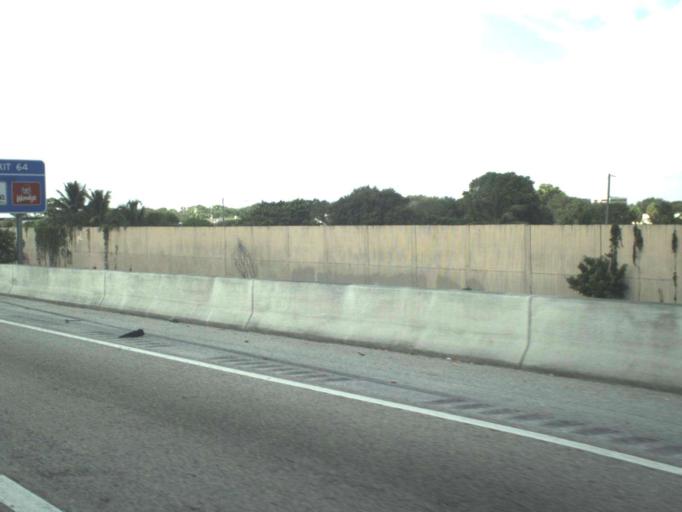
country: US
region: Florida
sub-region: Palm Beach County
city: Lake Clarke Shores
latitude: 26.6352
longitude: -80.0685
